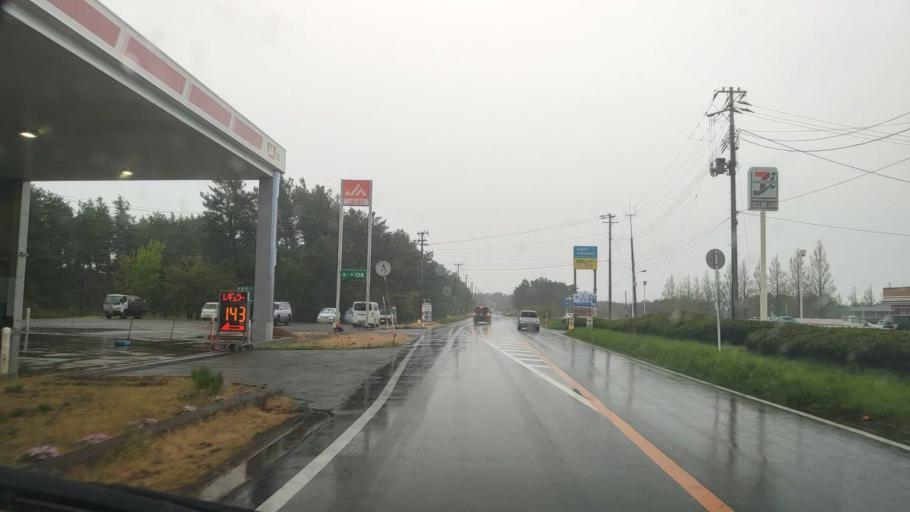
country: JP
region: Akita
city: Tenno
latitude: 40.0168
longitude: 139.9528
